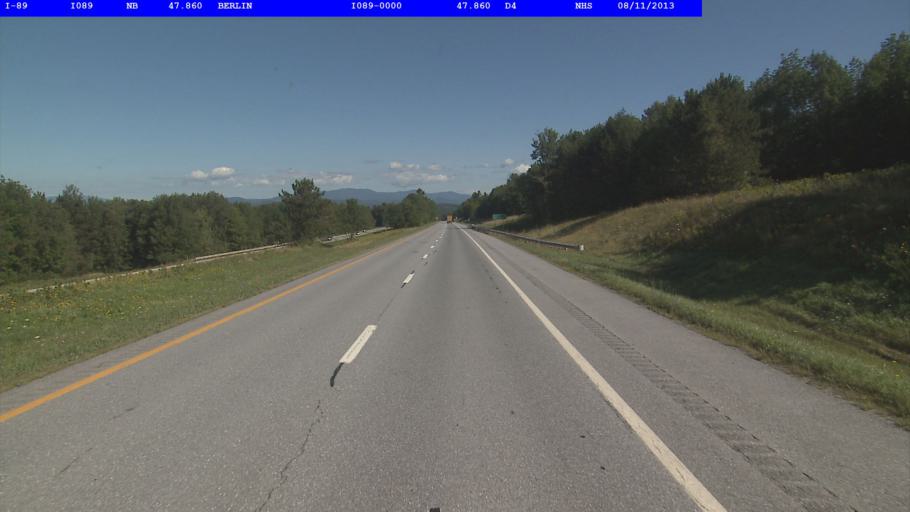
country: US
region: Vermont
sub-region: Orange County
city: Williamstown
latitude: 44.1812
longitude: -72.5756
